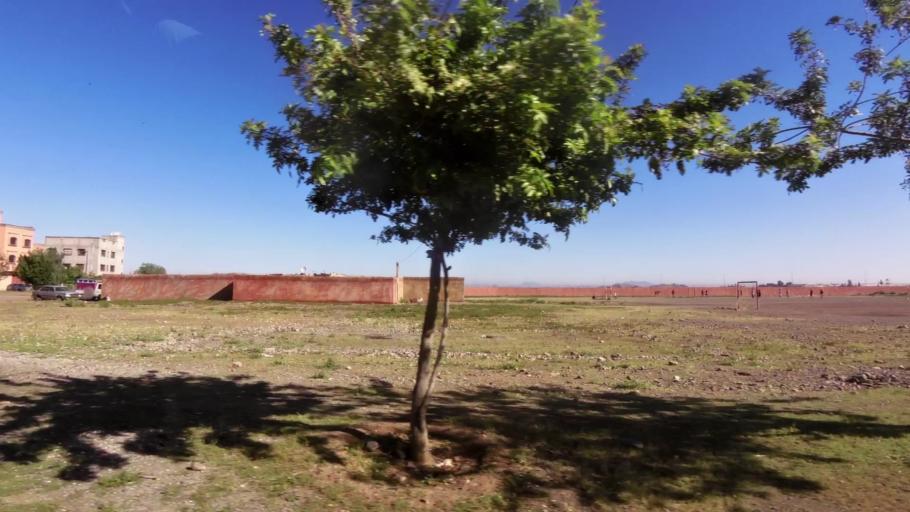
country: MA
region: Marrakech-Tensift-Al Haouz
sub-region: Marrakech
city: Marrakesh
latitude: 31.6021
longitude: -8.0353
